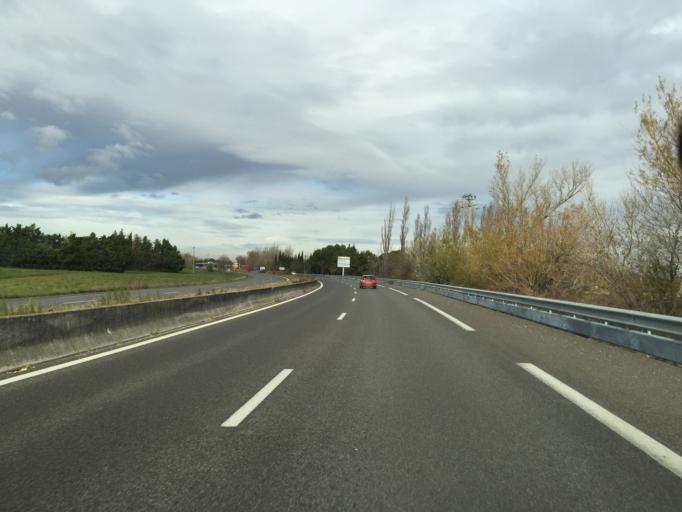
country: FR
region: Provence-Alpes-Cote d'Azur
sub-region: Departement du Vaucluse
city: Althen-des-Paluds
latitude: 44.0002
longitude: 4.9422
